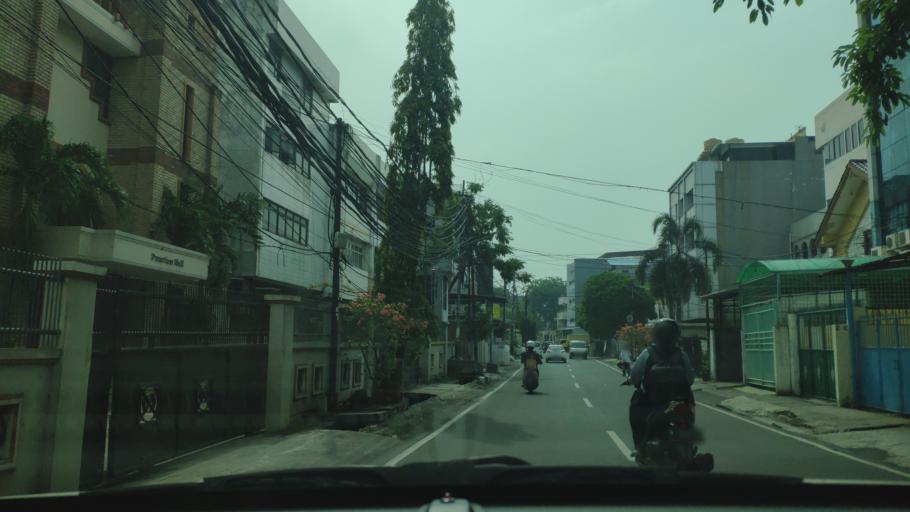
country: ID
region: Jakarta Raya
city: Jakarta
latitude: -6.1644
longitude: 106.8149
